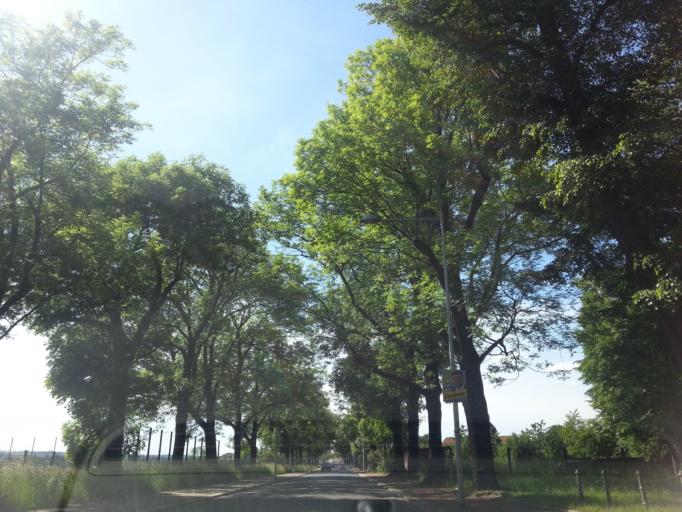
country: DE
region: Saxony
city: Dresden
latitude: 51.0664
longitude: 13.7242
